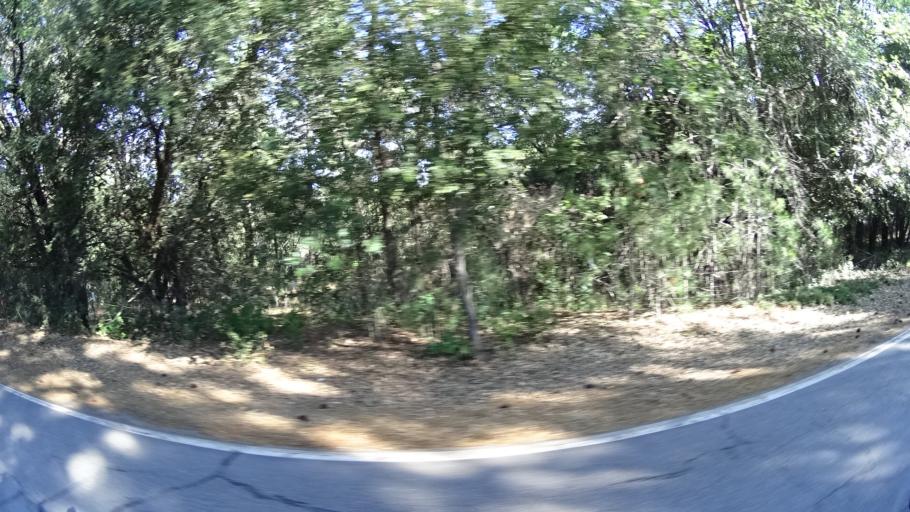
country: US
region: California
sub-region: Amador County
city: Pioneer
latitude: 38.3801
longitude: -120.5248
